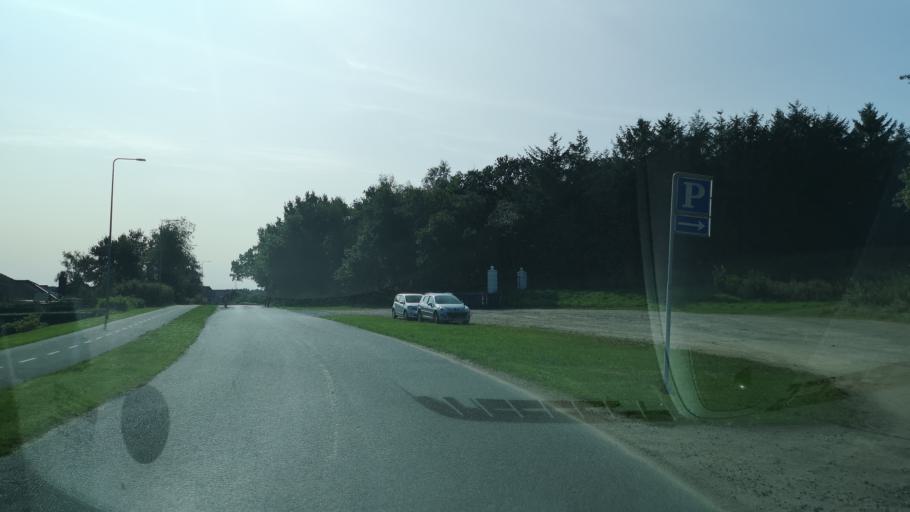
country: DK
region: Central Jutland
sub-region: Ringkobing-Skjern Kommune
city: Videbaek
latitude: 56.0814
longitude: 8.6182
